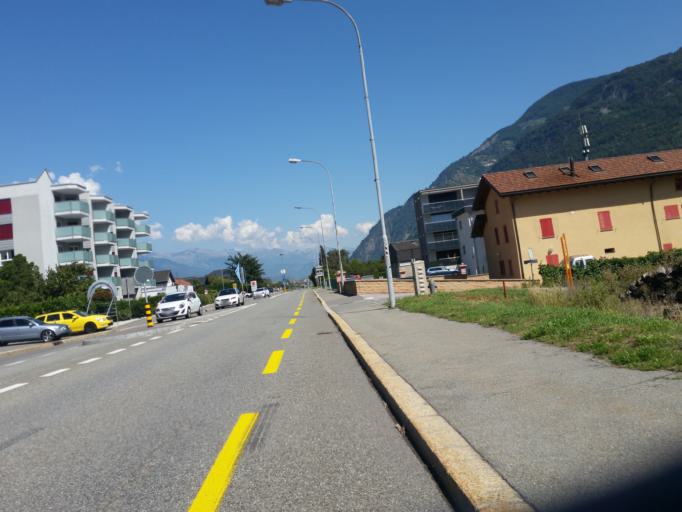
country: CH
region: Valais
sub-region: Martigny District
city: Saxon
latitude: 46.1530
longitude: 7.1826
